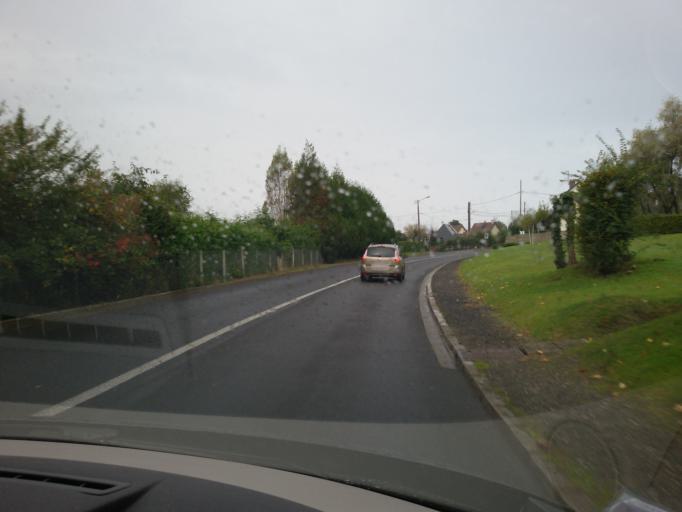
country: FR
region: Lower Normandy
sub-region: Departement du Calvados
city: Houlgate
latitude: 49.2979
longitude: -0.0663
